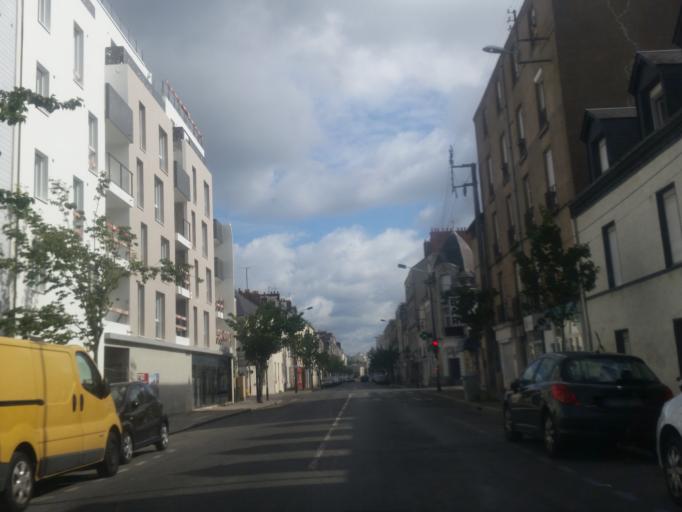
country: FR
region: Pays de la Loire
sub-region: Departement de la Loire-Atlantique
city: Nantes
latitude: 47.2215
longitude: -1.5312
